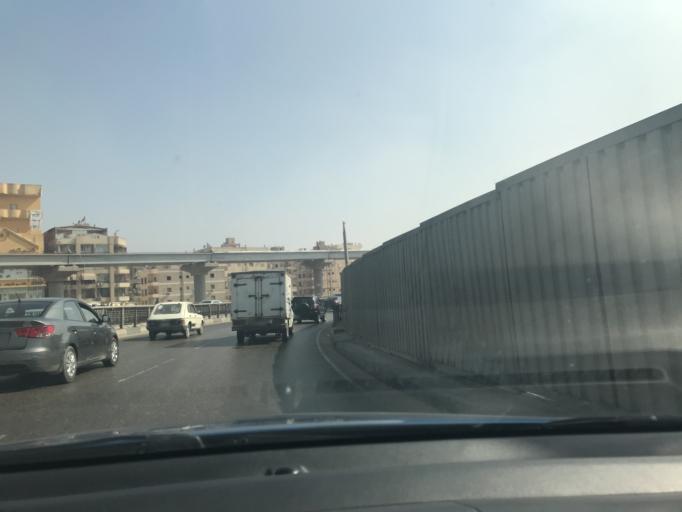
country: EG
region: Muhafazat al Qalyubiyah
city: Al Khankah
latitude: 30.1416
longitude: 31.4008
